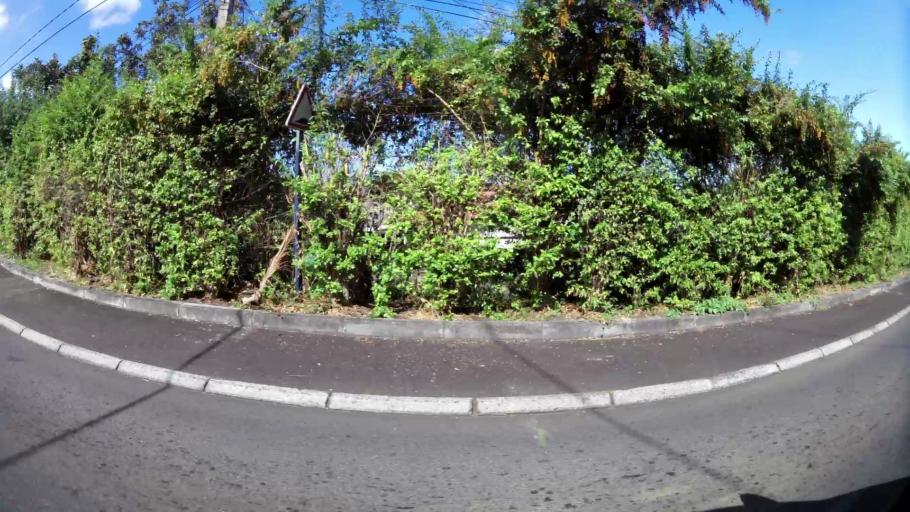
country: RE
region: Reunion
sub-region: Reunion
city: Le Tampon
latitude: -21.2864
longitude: 55.5139
